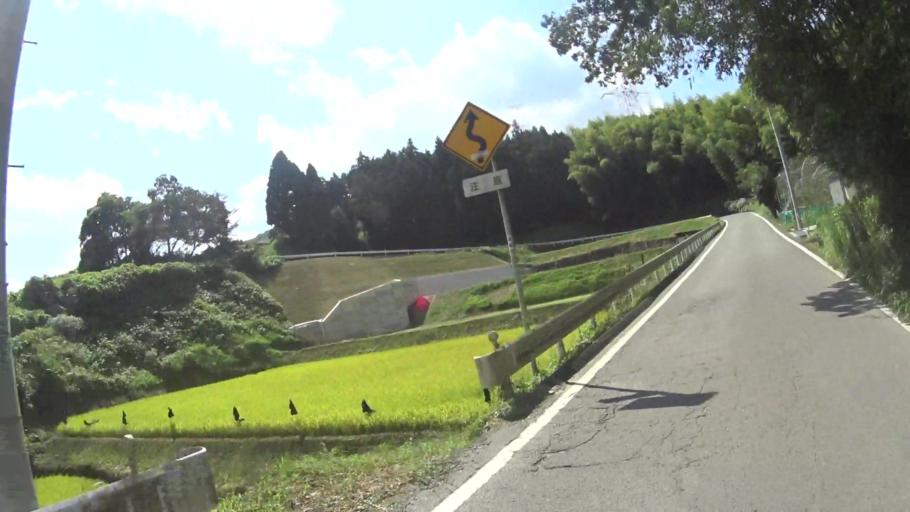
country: JP
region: Kyoto
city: Tanabe
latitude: 34.7679
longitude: 135.7473
